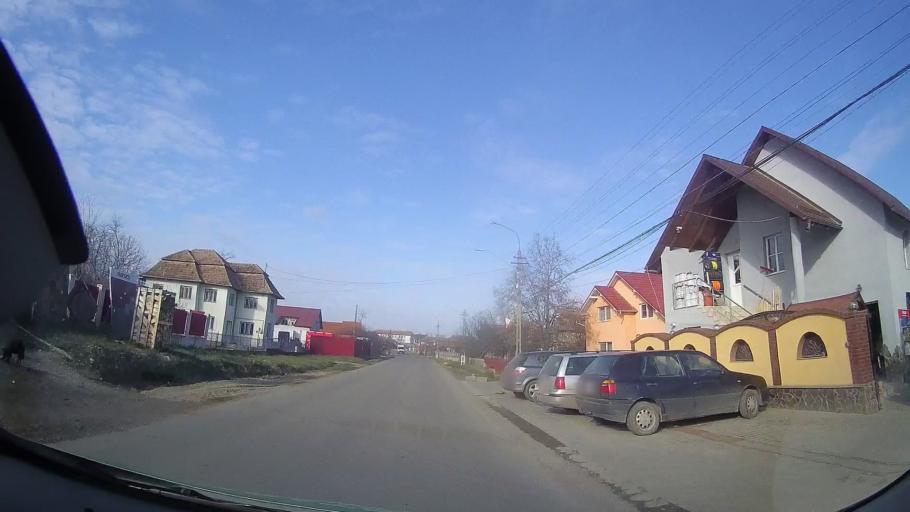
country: RO
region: Mures
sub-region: Comuna Valea Larga
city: Valea Larga
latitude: 46.6182
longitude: 24.0800
